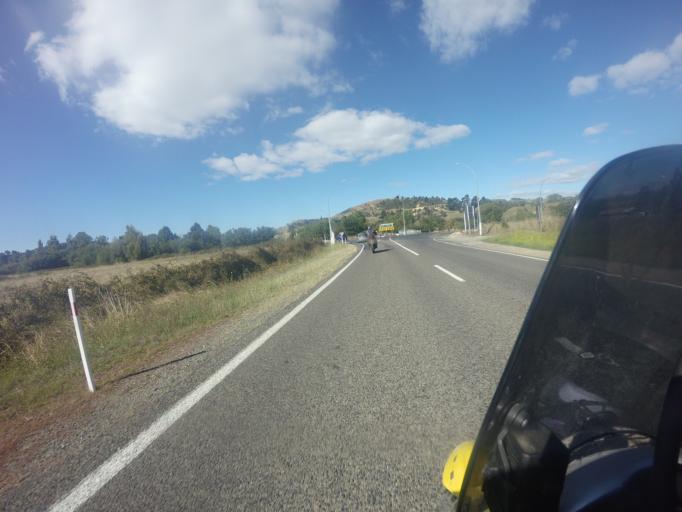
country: NZ
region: Bay of Plenty
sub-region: Opotiki District
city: Opotiki
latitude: -38.0584
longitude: 177.1289
